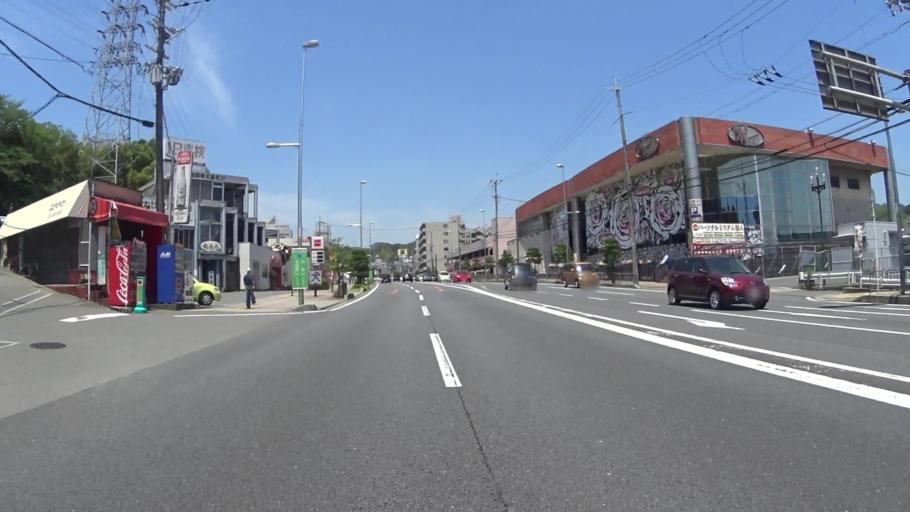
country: JP
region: Kyoto
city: Kameoka
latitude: 35.0679
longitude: 135.5357
